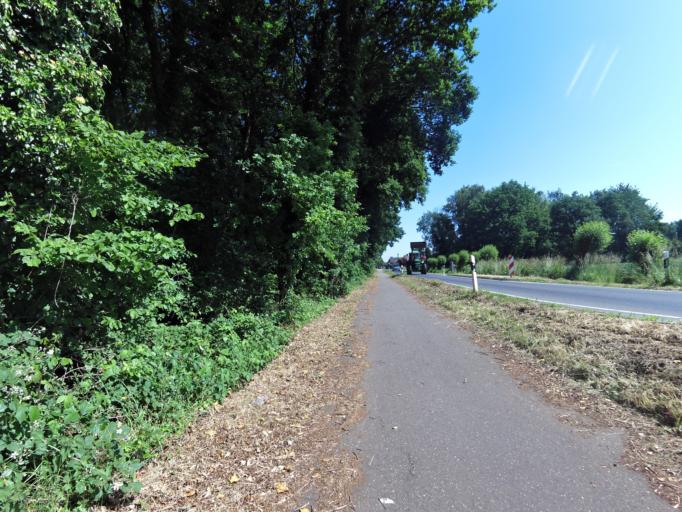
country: DE
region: North Rhine-Westphalia
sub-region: Regierungsbezirk Koln
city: Gangelt
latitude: 50.9789
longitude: 6.0253
